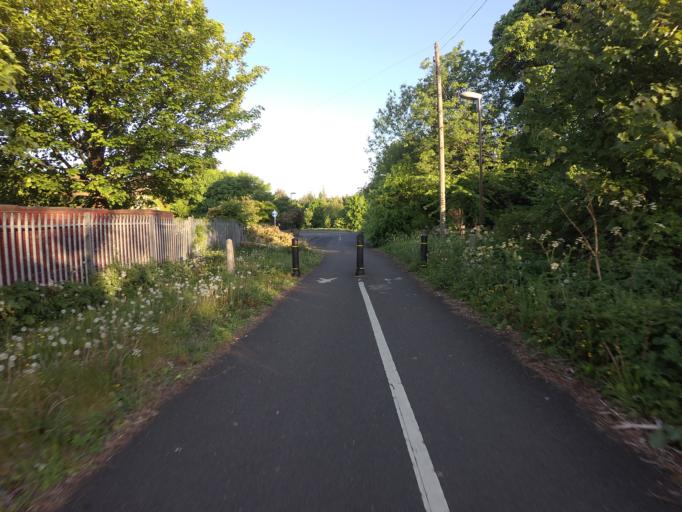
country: GB
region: Scotland
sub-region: West Lothian
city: Livingston
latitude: 55.8964
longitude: -3.5631
